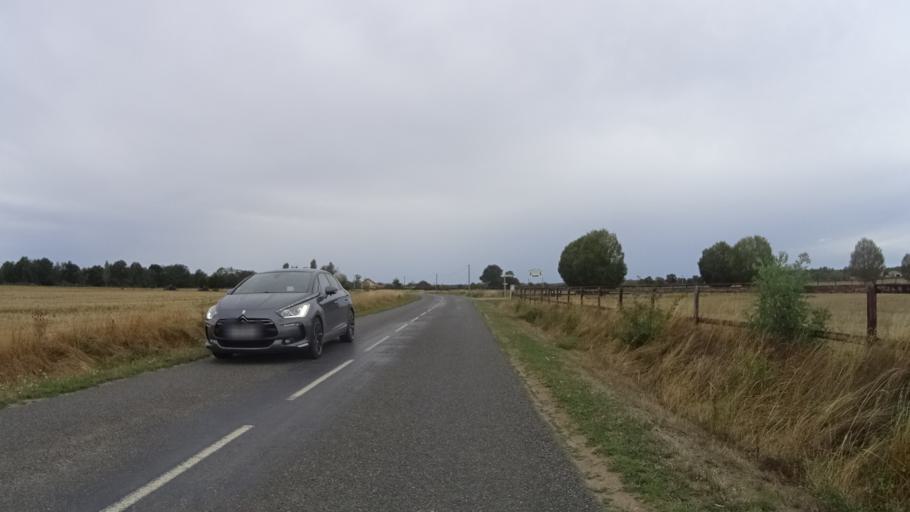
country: FR
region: Bourgogne
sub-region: Departement de la Nievre
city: Decize
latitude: 46.7852
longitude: 3.5296
